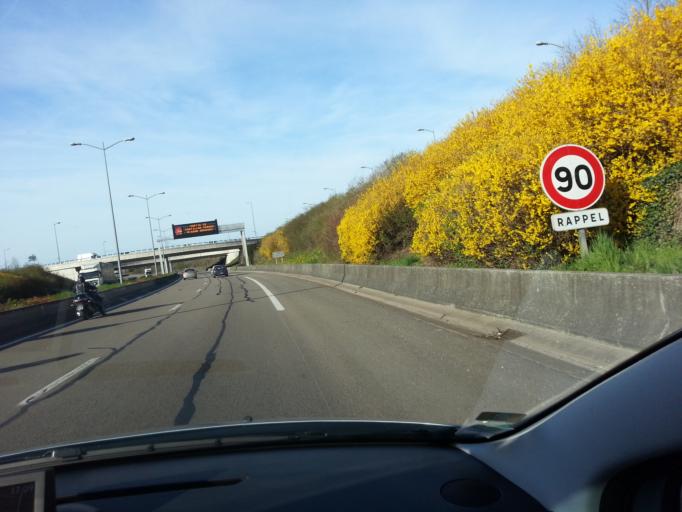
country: FR
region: Franche-Comte
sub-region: Departement du Doubs
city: Besancon
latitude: 47.2605
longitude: 6.0046
